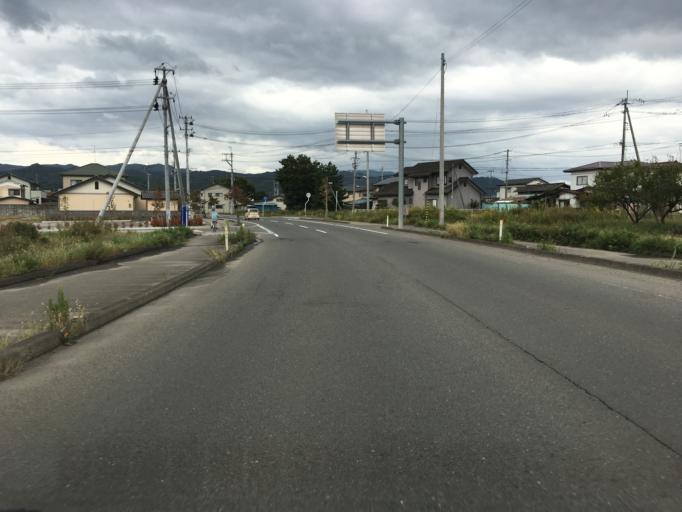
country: JP
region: Fukushima
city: Yanagawamachi-saiwaicho
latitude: 37.8569
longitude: 140.5989
